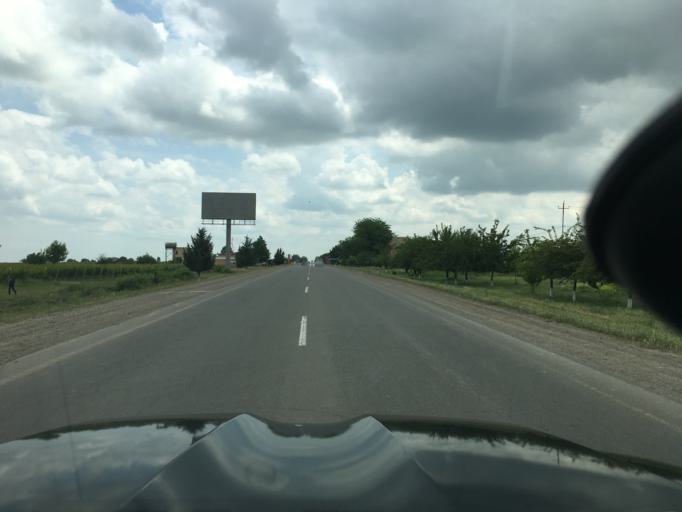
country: AZ
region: Tovuz
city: Tovuz
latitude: 40.9721
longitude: 45.6847
